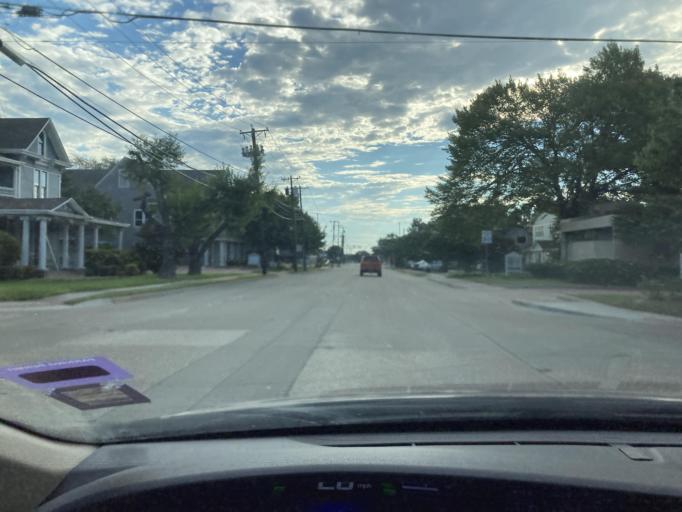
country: US
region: Texas
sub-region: Collin County
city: Plano
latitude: 33.0239
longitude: -96.7029
